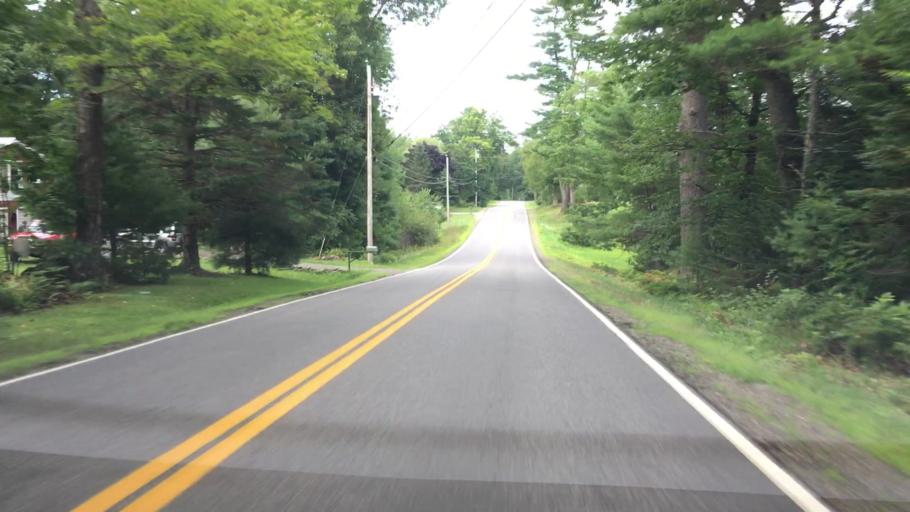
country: US
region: Maine
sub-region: Waldo County
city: Lincolnville
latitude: 44.3242
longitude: -69.0671
